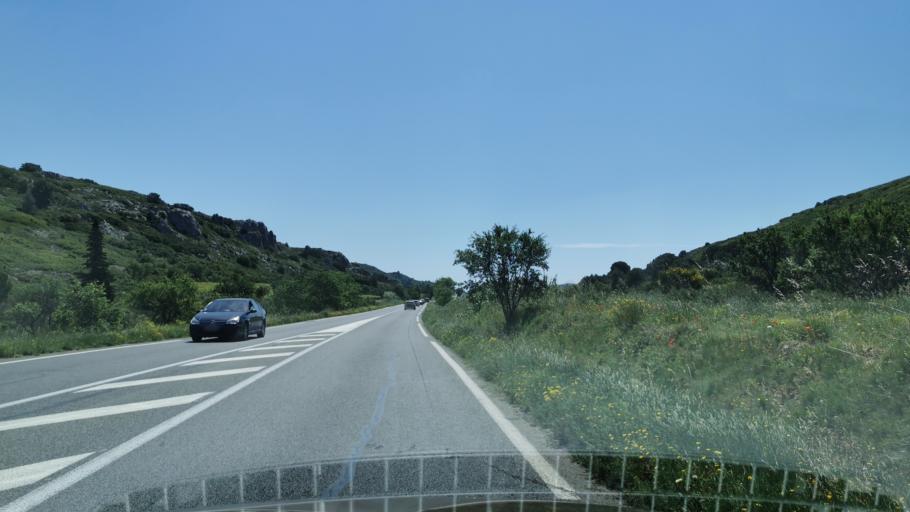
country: FR
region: Languedoc-Roussillon
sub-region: Departement de l'Aude
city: Nevian
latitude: 43.2065
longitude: 2.8849
